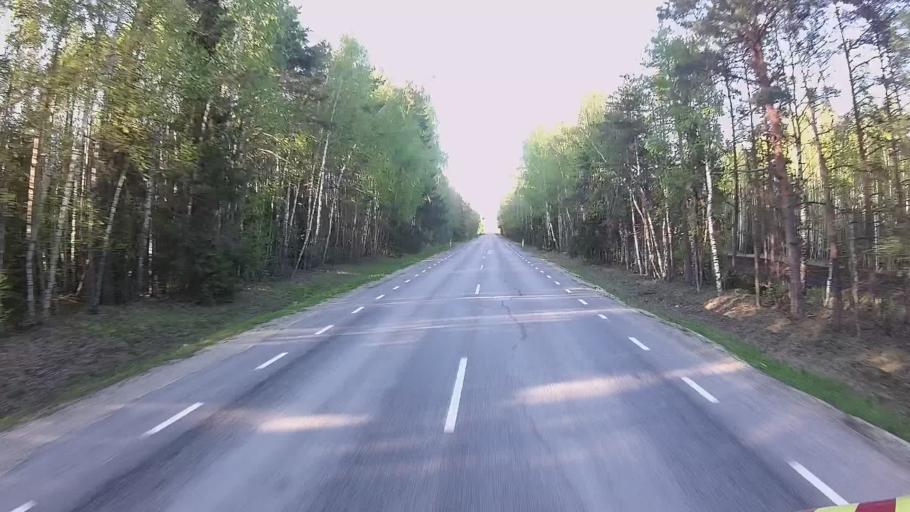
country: EE
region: Jogevamaa
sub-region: Poltsamaa linn
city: Poltsamaa
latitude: 58.4867
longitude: 25.8218
